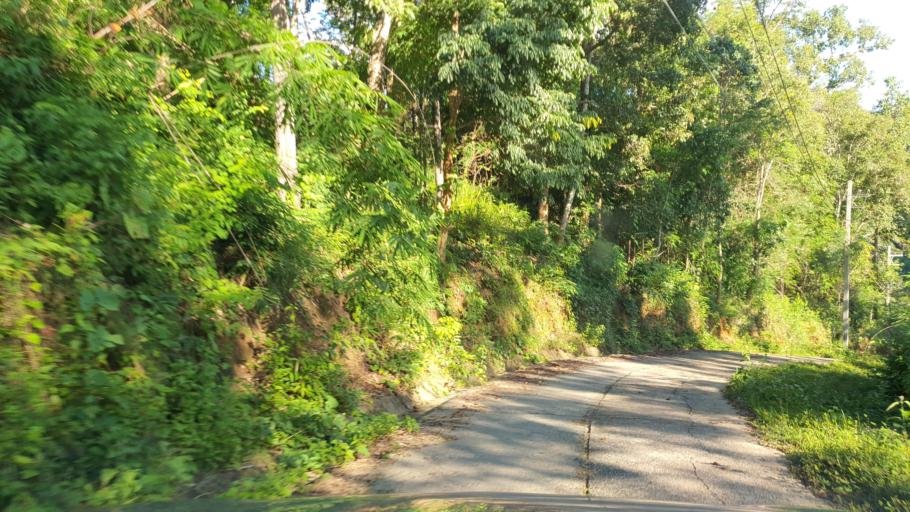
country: TH
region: Chiang Mai
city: Mae On
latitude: 18.8111
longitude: 99.3279
